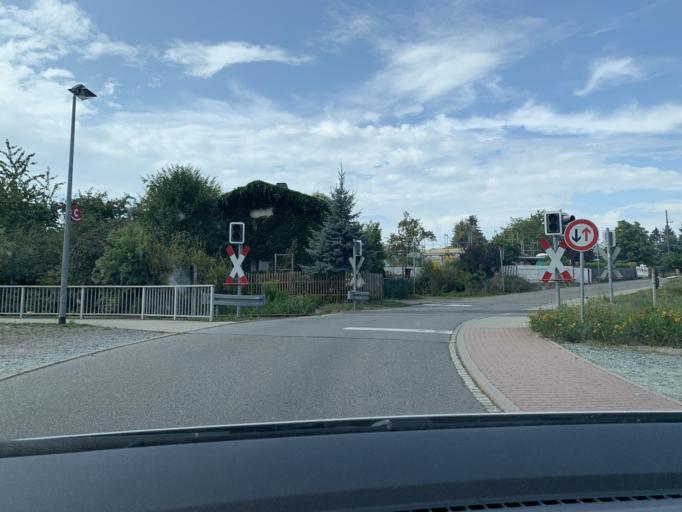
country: DE
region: Saxony
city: Frankenberg
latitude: 50.9270
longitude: 13.0691
